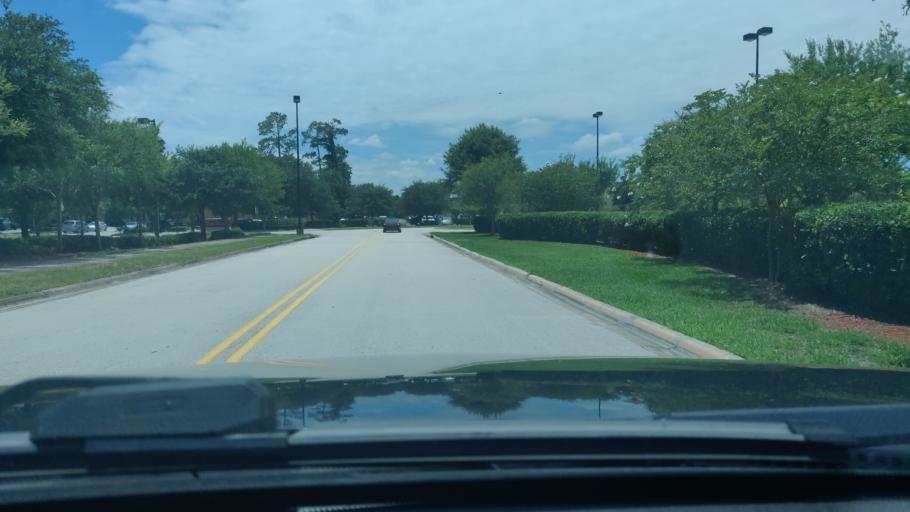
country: US
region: Florida
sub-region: Flagler County
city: Palm Coast
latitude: 29.5545
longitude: -81.2238
